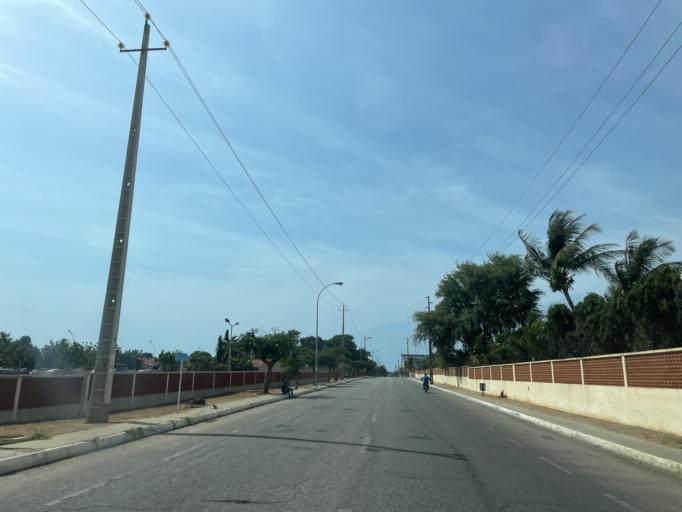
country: AO
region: Luanda
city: Luanda
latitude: -8.9131
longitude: 13.1846
